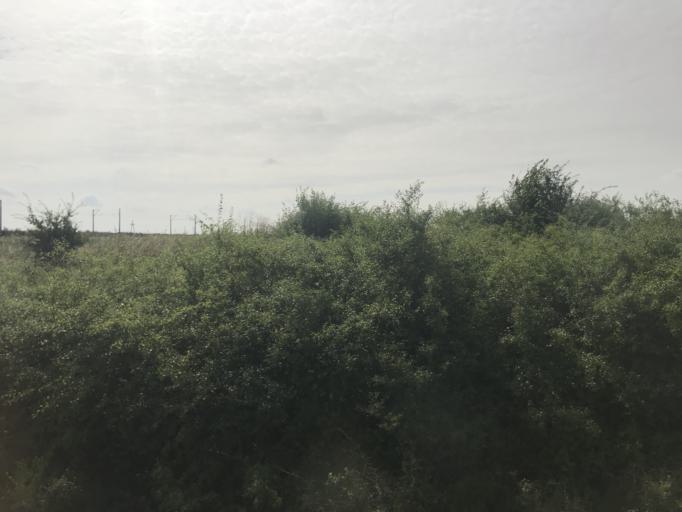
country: PL
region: Kujawsko-Pomorskie
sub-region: Powiat inowroclawski
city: Inowroclaw
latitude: 52.7850
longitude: 18.1943
